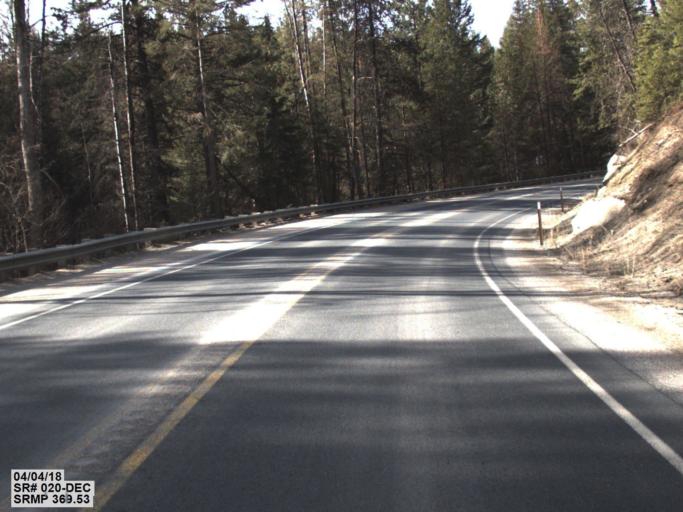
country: US
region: Washington
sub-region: Stevens County
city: Chewelah
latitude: 48.5140
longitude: -117.6537
